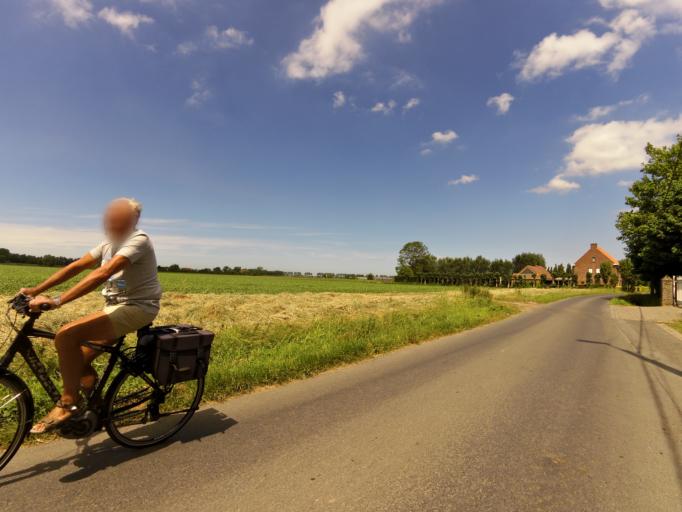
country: BE
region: Flanders
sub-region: Provincie West-Vlaanderen
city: Ichtegem
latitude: 51.1359
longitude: 3.0059
